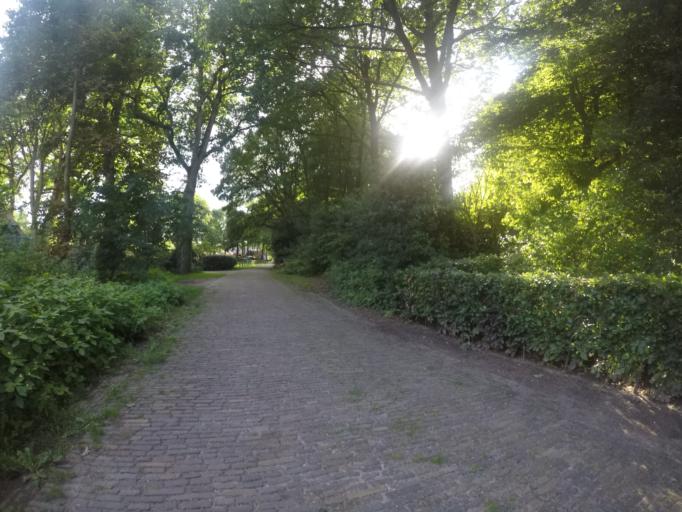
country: NL
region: Drenthe
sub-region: Gemeente Westerveld
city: Dwingeloo
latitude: 52.8569
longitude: 6.3231
